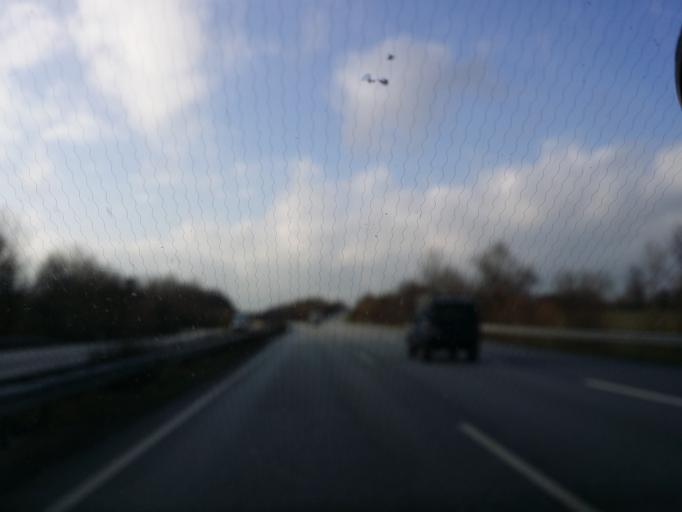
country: DE
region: Schleswig-Holstein
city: Bredenbek
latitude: 54.3168
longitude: 9.8607
